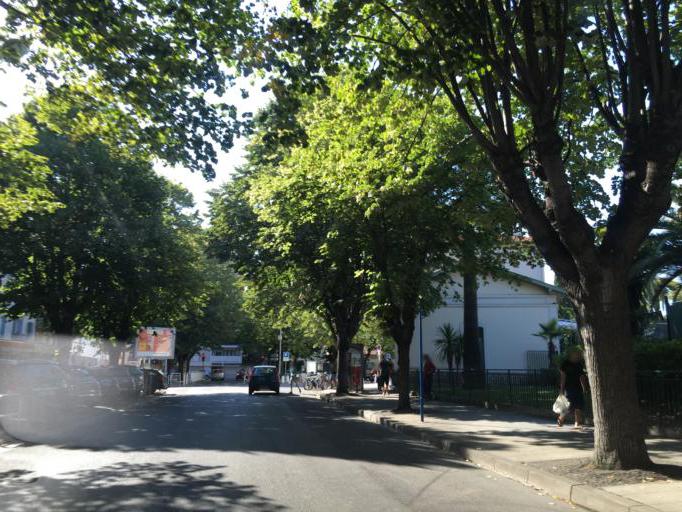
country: FR
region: Provence-Alpes-Cote d'Azur
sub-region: Departement des Alpes-Maritimes
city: Villefranche-sur-Mer
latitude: 43.7052
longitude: 7.2907
